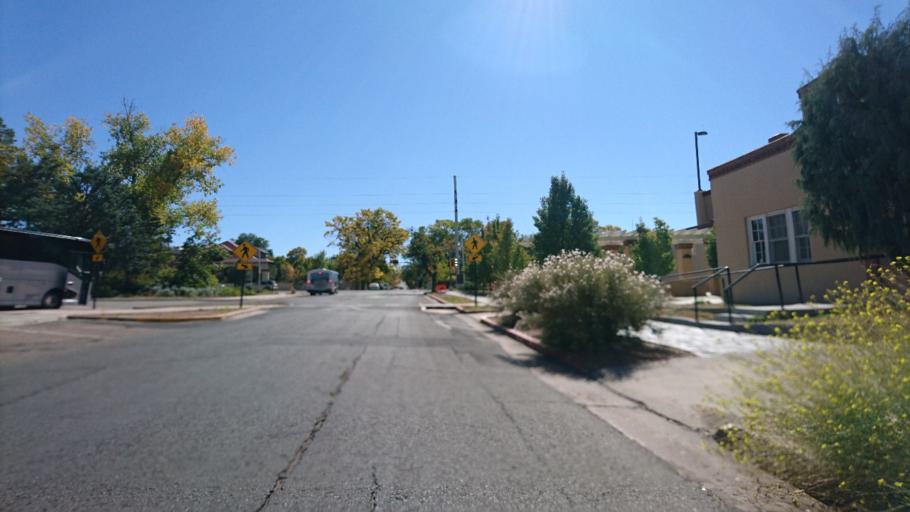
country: US
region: New Mexico
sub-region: Santa Fe County
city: Santa Fe
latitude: 35.6825
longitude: -105.9408
